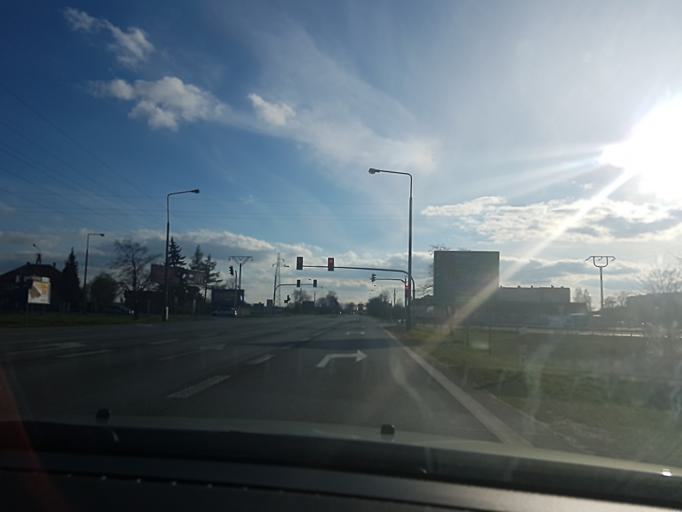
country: PL
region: Lodz Voivodeship
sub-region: Powiat kutnowski
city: Kutno
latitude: 52.2152
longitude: 19.3815
